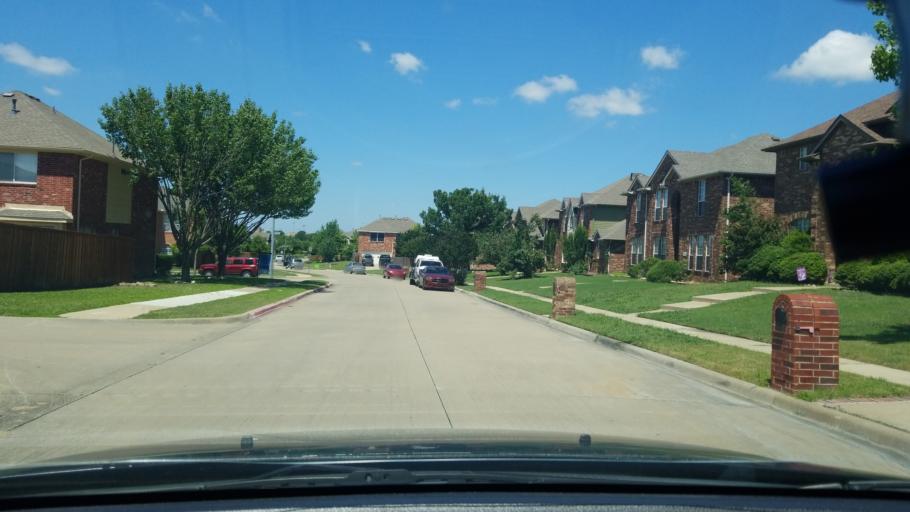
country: US
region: Texas
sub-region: Dallas County
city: Sunnyvale
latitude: 32.8082
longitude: -96.5982
